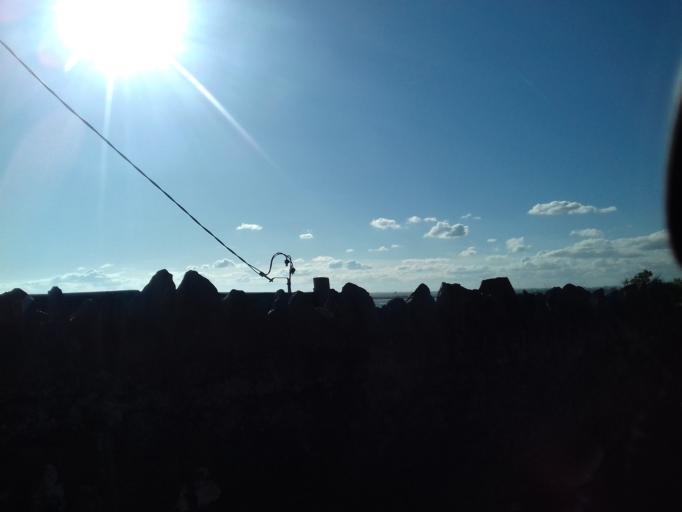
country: IE
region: Leinster
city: Sutton
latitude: 53.3767
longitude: -6.1016
